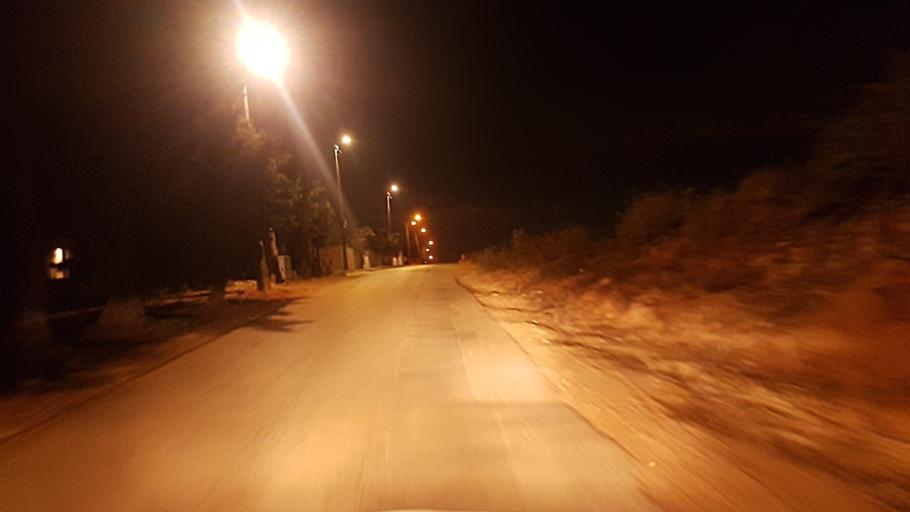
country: IL
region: Central District
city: Hod HaSharon
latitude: 32.1600
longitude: 34.8722
